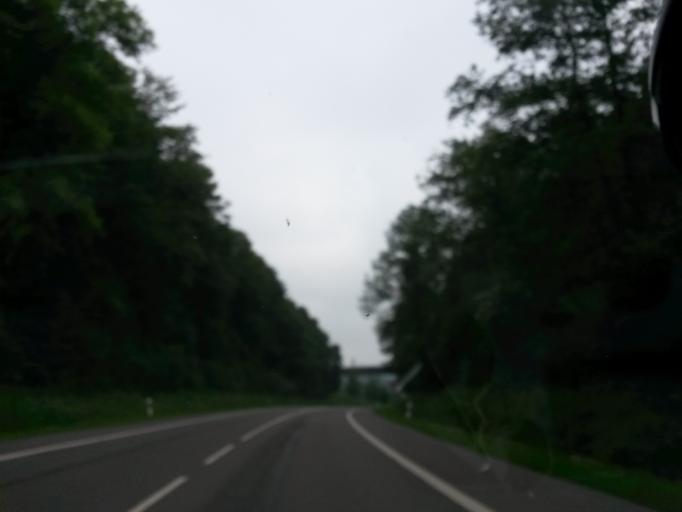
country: DE
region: North Rhine-Westphalia
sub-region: Regierungsbezirk Koln
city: Engelskirchen
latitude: 50.9793
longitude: 7.4329
